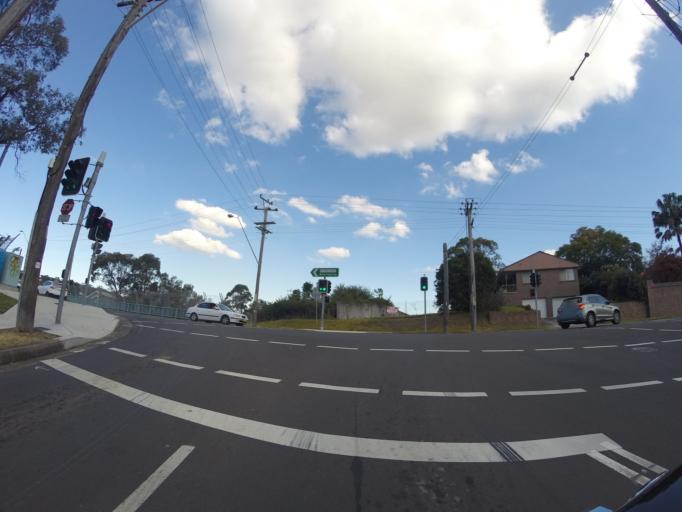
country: AU
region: New South Wales
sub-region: Wollongong
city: West Wollongong
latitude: -34.4240
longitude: 150.8683
